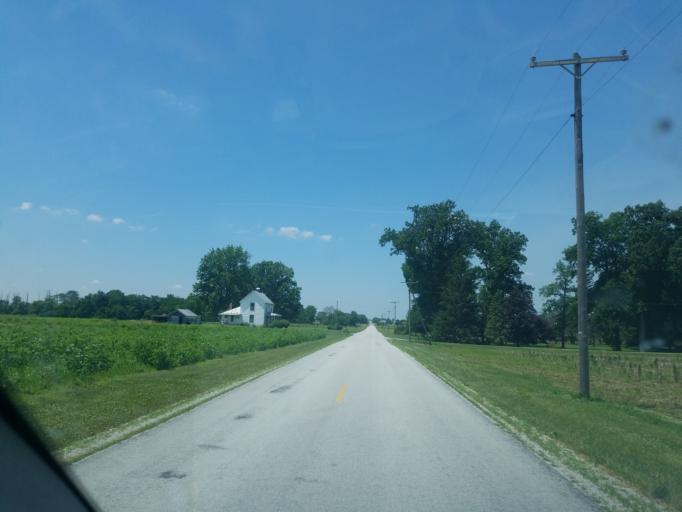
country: US
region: Ohio
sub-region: Hardin County
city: Kenton
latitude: 40.7314
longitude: -83.6157
